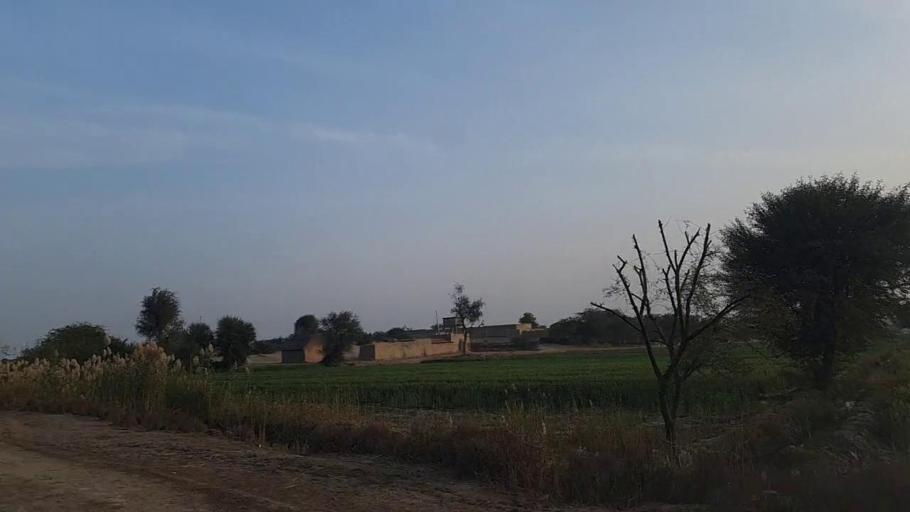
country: PK
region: Sindh
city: Jam Sahib
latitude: 26.4096
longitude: 68.6056
